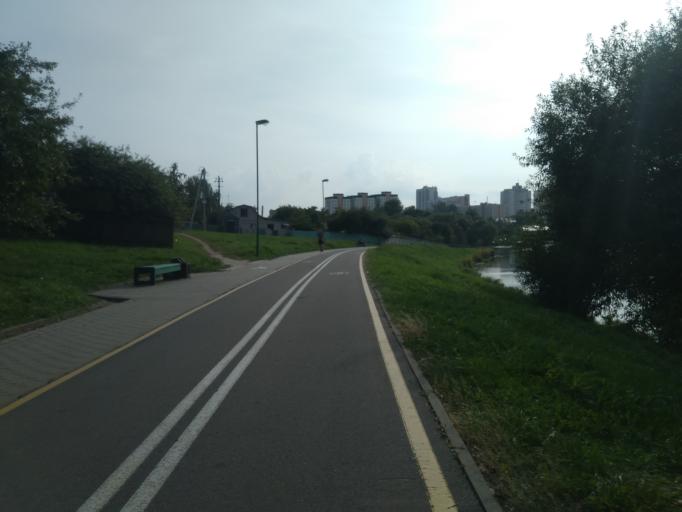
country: BY
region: Minsk
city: Minsk
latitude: 53.8793
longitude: 27.5748
